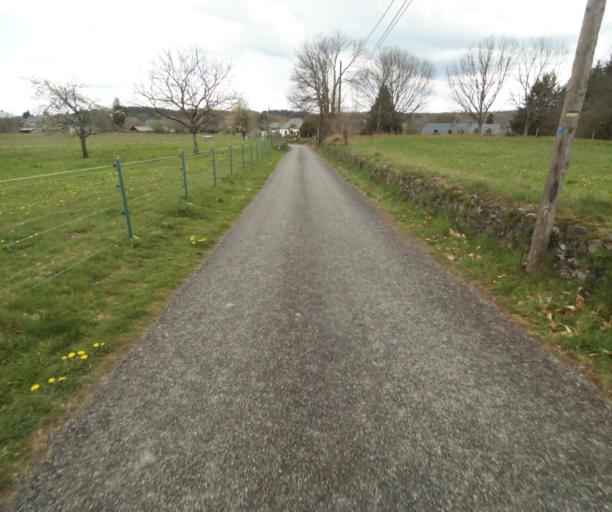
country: FR
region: Limousin
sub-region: Departement de la Correze
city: Laguenne
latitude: 45.2459
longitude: 1.8953
